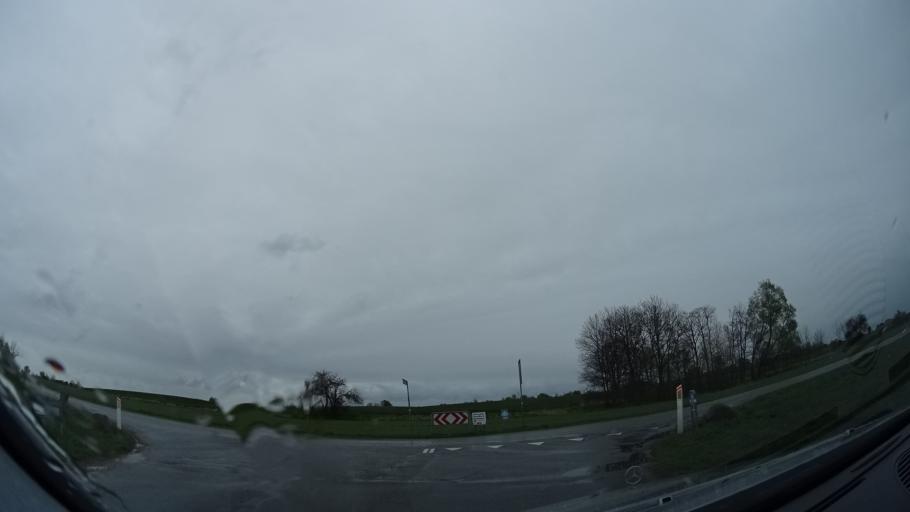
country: DK
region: Zealand
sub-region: Lejre Kommune
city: Ejby
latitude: 55.7044
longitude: 11.8735
